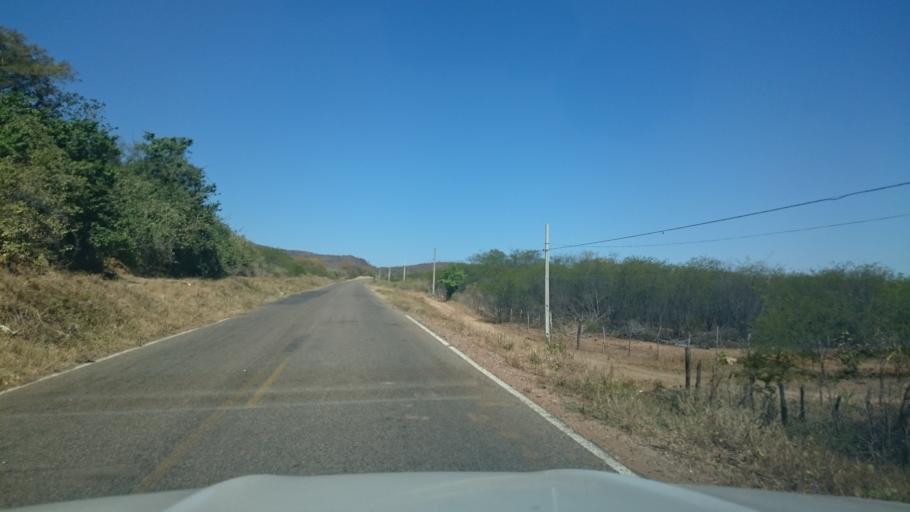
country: BR
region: Paraiba
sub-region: Catole Do Rocha
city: Sao Bento
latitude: -6.1537
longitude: -37.8329
